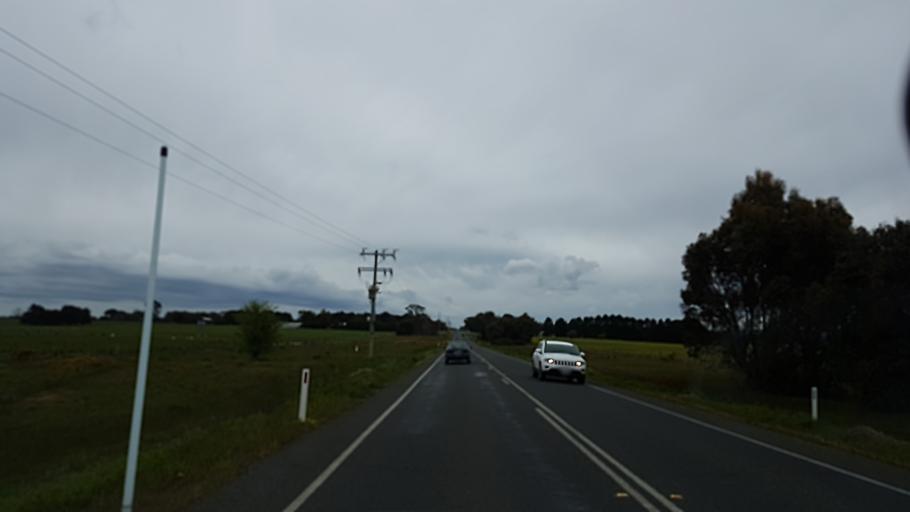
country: AU
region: Victoria
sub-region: Moorabool
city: Bacchus Marsh
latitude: -37.6085
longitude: 144.2127
